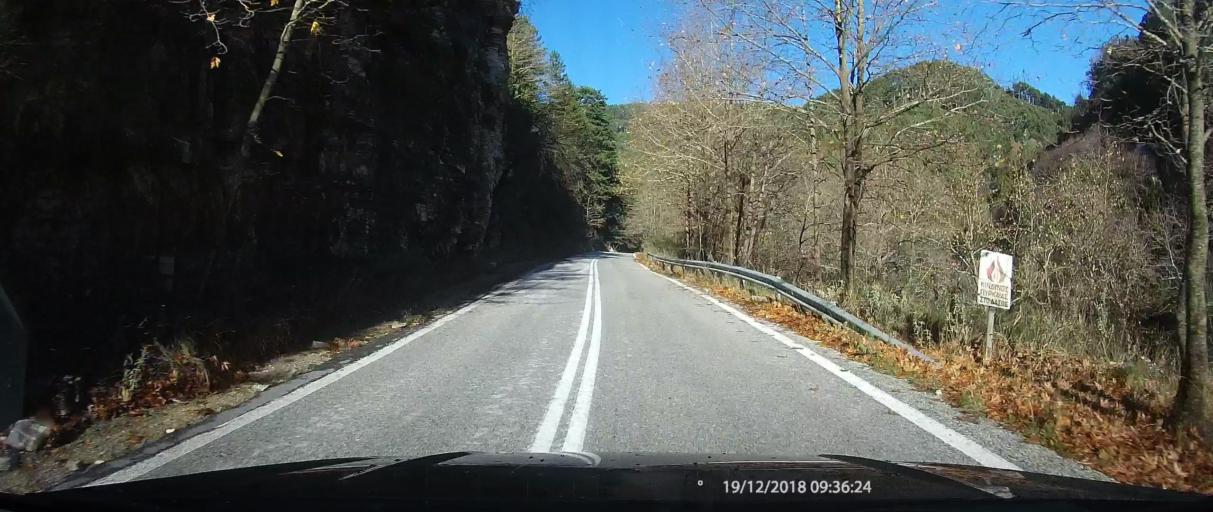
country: GR
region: Peloponnese
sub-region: Nomos Lakonias
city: Magoula
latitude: 37.0822
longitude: 22.2827
